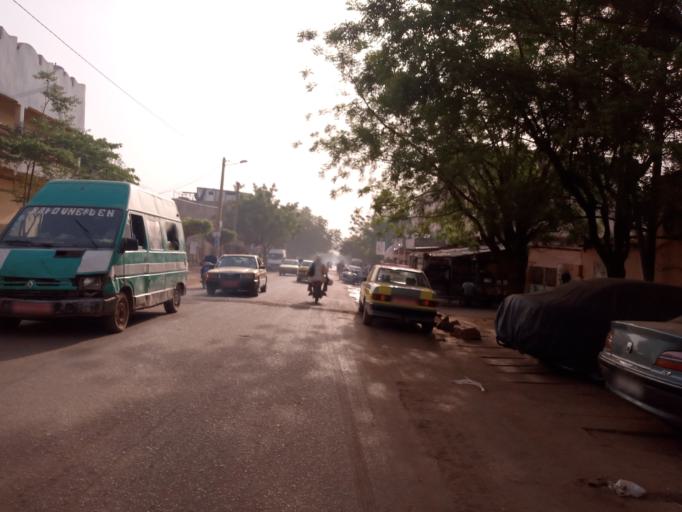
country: ML
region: Bamako
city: Bamako
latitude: 12.6648
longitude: -7.9746
